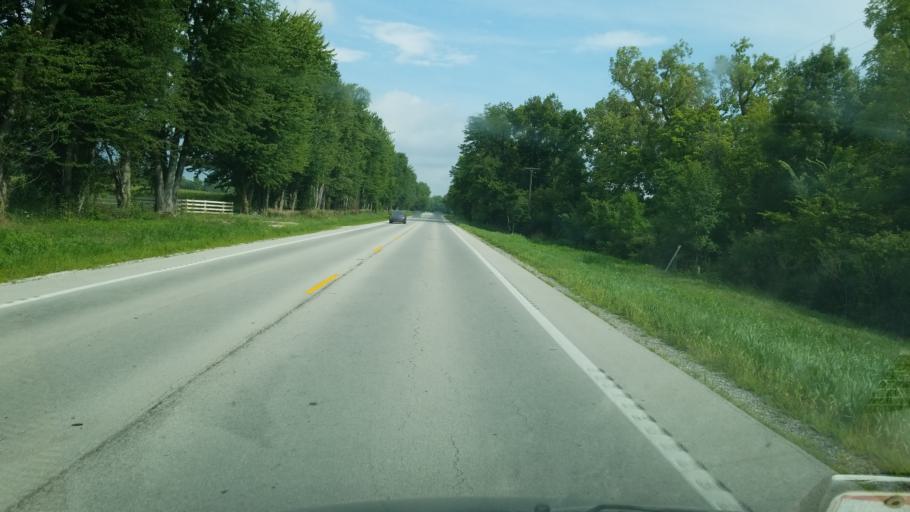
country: US
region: Ohio
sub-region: Sandusky County
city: Ballville
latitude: 41.2713
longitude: -83.1685
